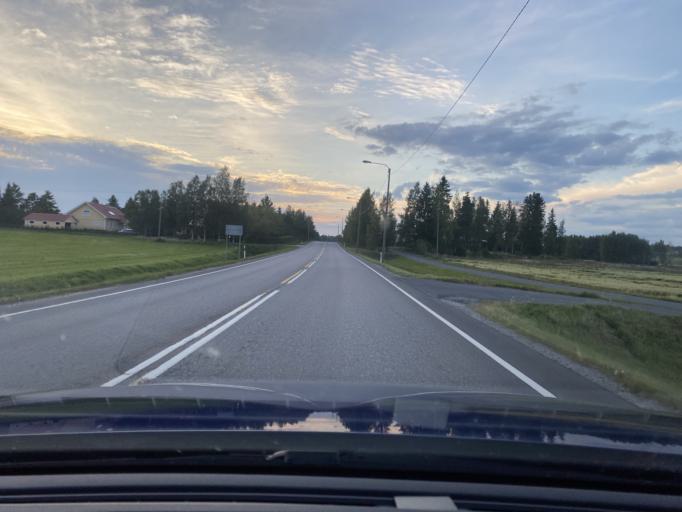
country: FI
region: Satakunta
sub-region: Pohjois-Satakunta
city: Kankaanpaeae
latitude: 61.7458
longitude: 22.5224
